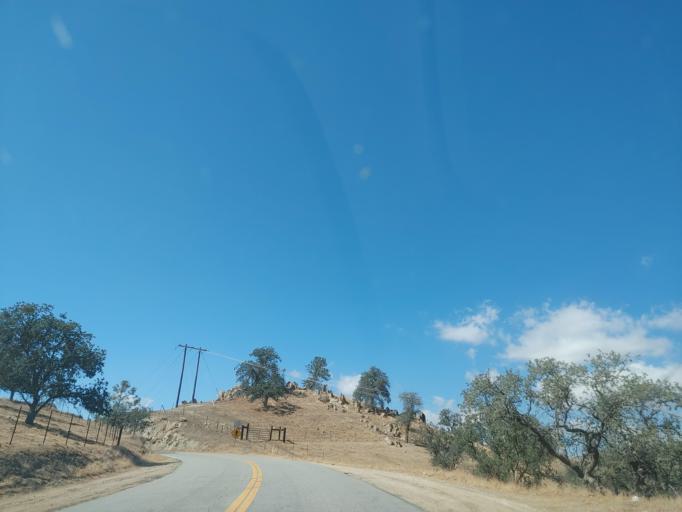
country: US
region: California
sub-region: Kern County
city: Golden Hills
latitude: 35.1947
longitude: -118.5320
